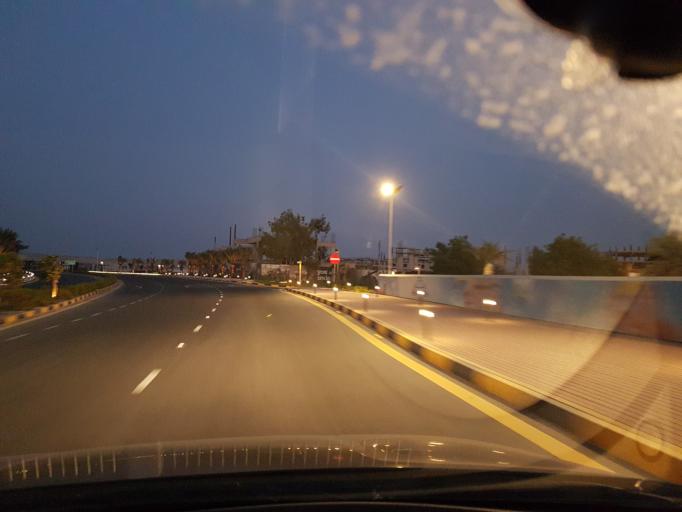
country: BH
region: Central Governorate
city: Dar Kulayb
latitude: 26.0156
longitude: 50.5102
